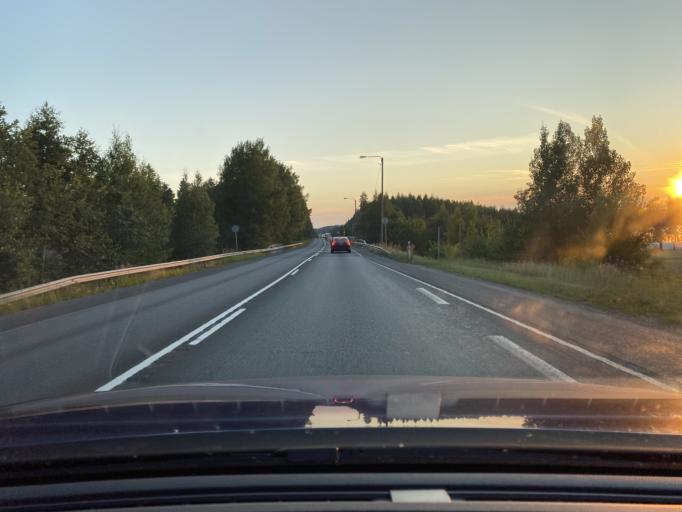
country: FI
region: Pirkanmaa
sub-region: Luoteis-Pirkanmaa
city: Ikaalinen
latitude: 61.7560
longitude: 23.0520
